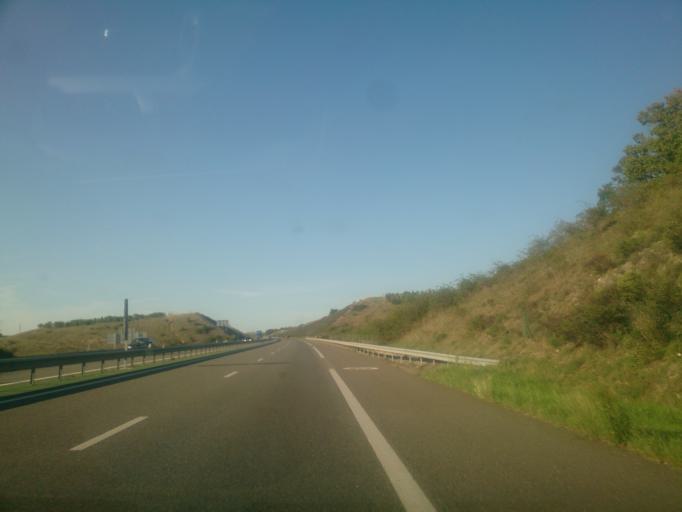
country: FR
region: Midi-Pyrenees
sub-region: Departement du Lot
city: Cahors
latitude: 44.5191
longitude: 1.5084
